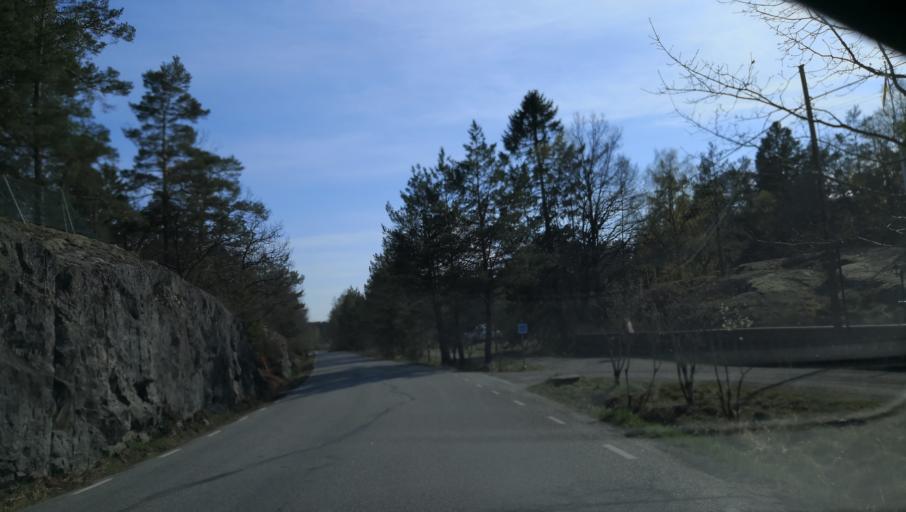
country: SE
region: Stockholm
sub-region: Varmdo Kommun
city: Holo
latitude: 59.3005
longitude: 18.6163
